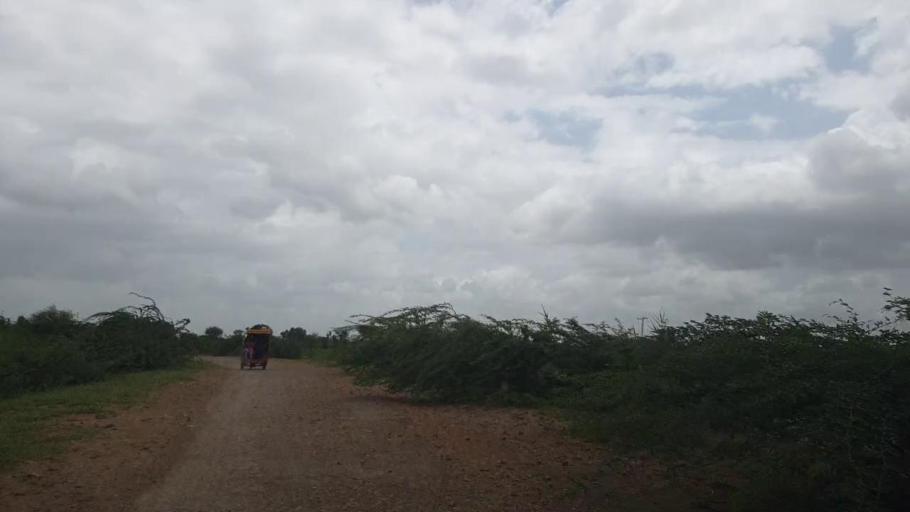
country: PK
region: Sindh
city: Badin
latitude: 24.6413
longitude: 68.9476
